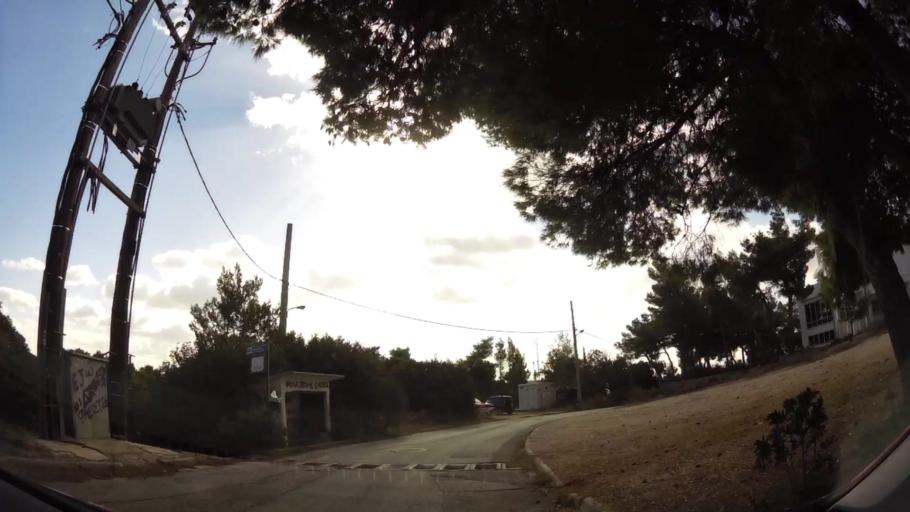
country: GR
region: Attica
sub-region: Nomarchia Anatolikis Attikis
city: Thrakomakedones
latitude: 38.1439
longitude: 23.7581
